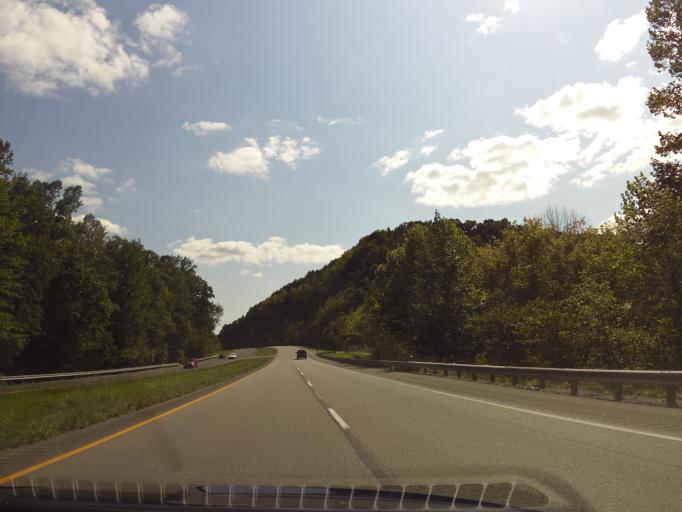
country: US
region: Kentucky
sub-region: Bell County
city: Pineville
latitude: 36.6849
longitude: -83.6843
